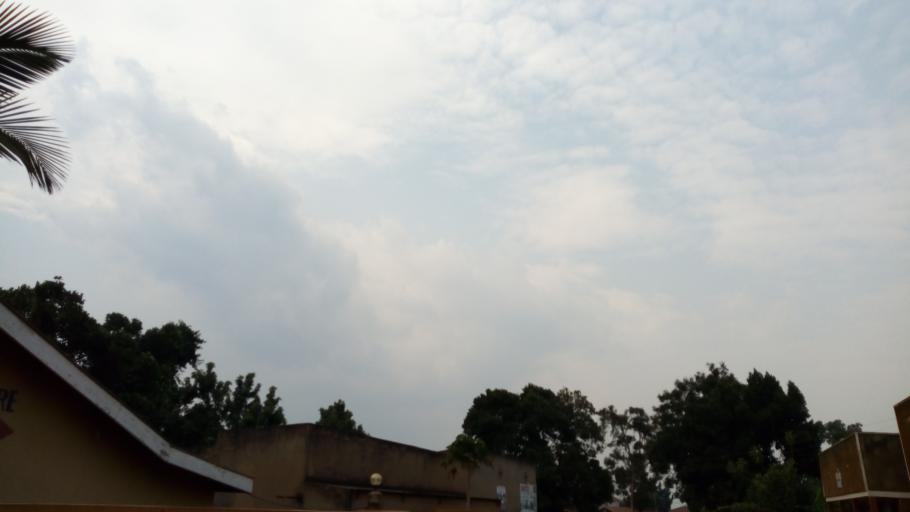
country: UG
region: Central Region
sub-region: Wakiso District
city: Kireka
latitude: 0.3200
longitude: 32.6385
